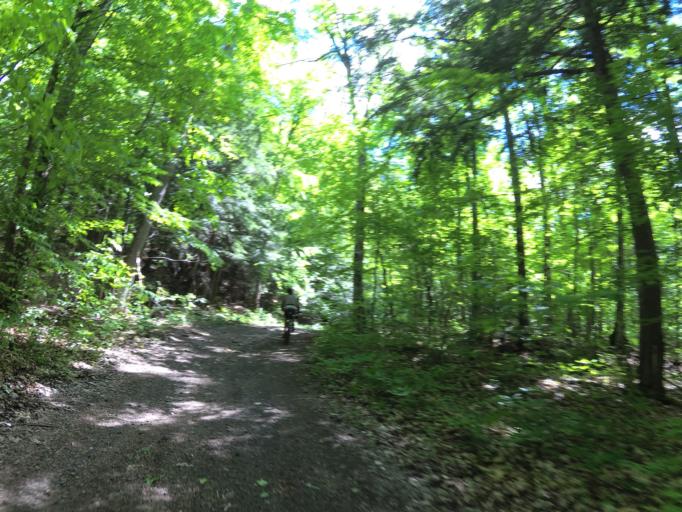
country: CA
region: Ontario
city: Renfrew
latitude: 45.0519
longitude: -76.8383
